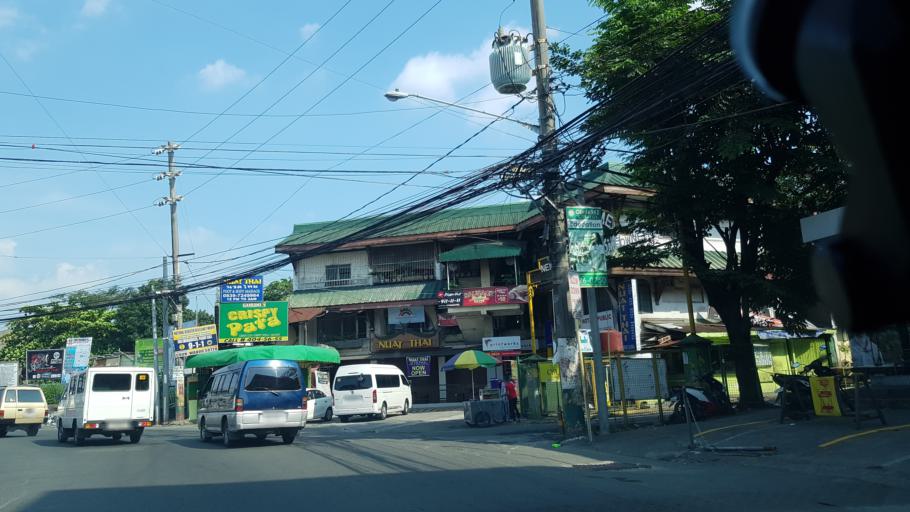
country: PH
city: Sambayanihan People's Village
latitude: 14.4824
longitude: 121.0367
